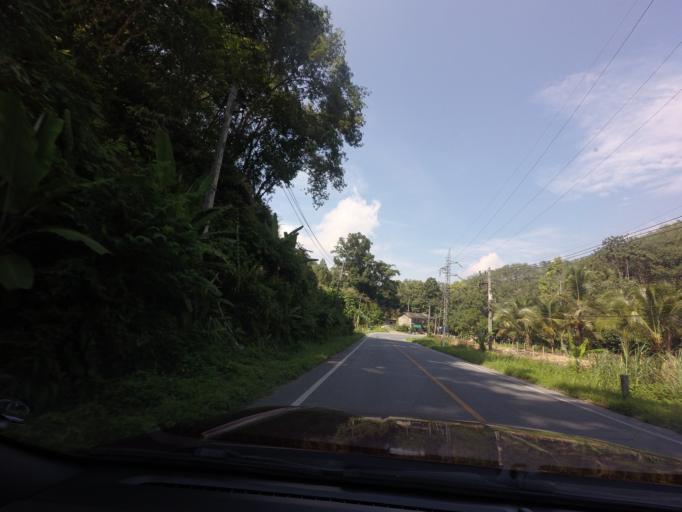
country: TH
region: Yala
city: Betong
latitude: 5.8883
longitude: 101.1461
